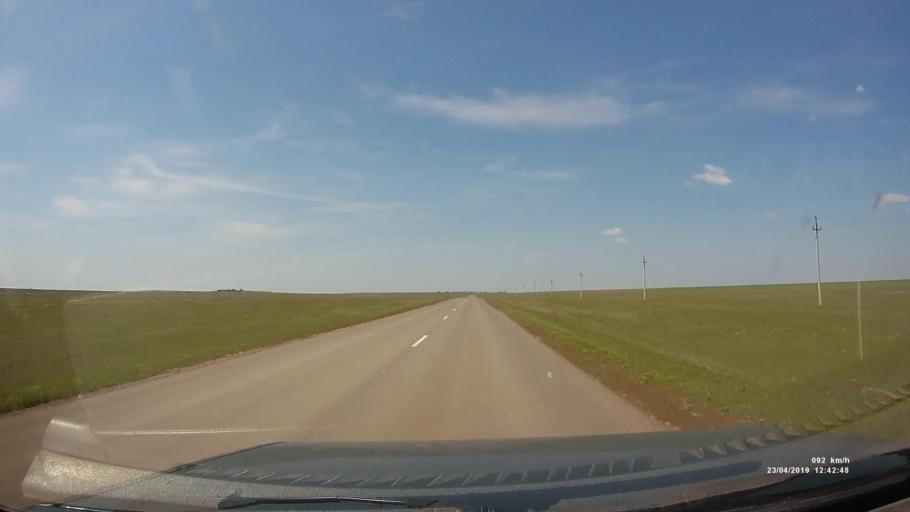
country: RU
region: Kalmykiya
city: Yashalta
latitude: 46.4587
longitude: 42.6601
